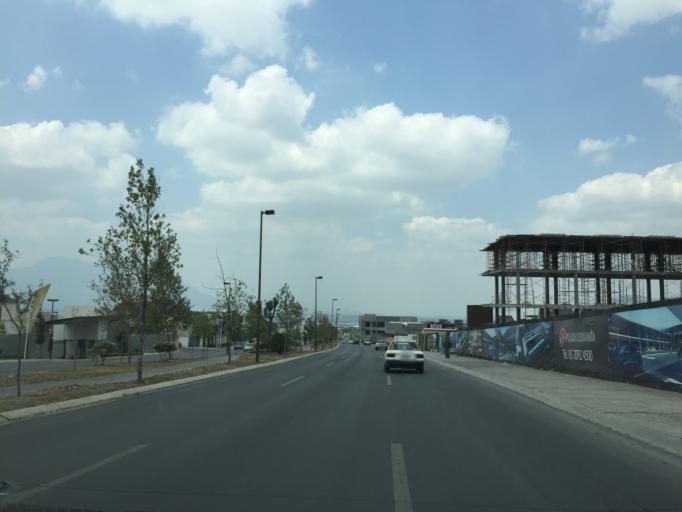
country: MX
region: Nuevo Leon
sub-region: Garcia
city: Mitras Poniente
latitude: 25.7448
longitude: -100.4200
